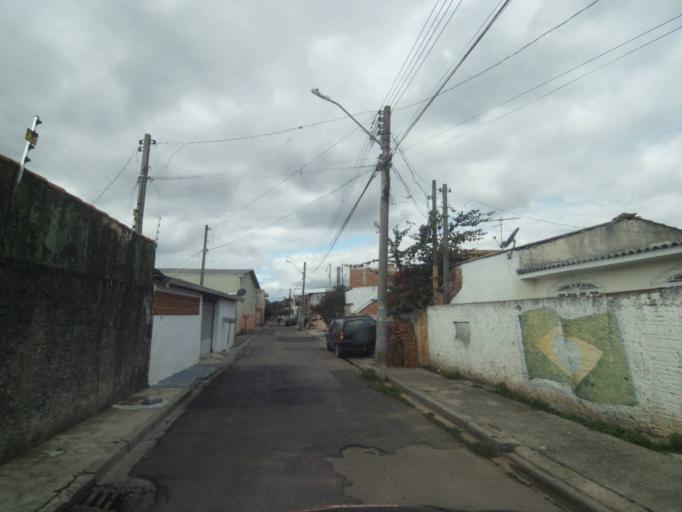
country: BR
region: Parana
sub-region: Sao Jose Dos Pinhais
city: Sao Jose dos Pinhais
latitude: -25.5505
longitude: -49.2508
